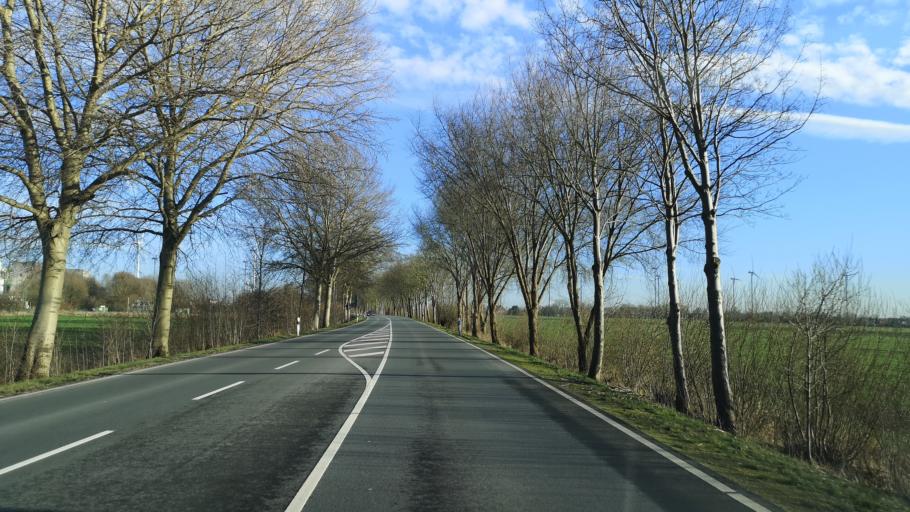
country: DE
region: Schleswig-Holstein
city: Lagerdorf
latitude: 53.8714
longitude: 9.5766
